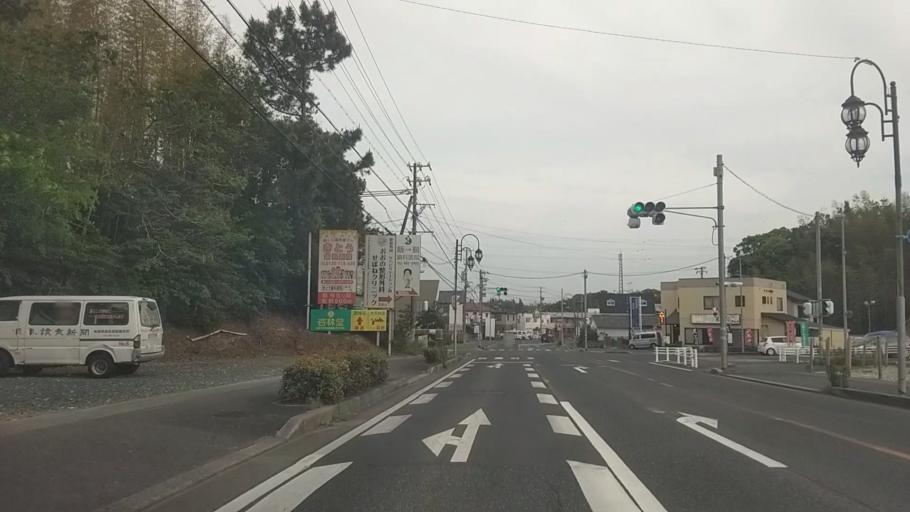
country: JP
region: Shizuoka
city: Hamamatsu
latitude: 34.7308
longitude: 137.6898
